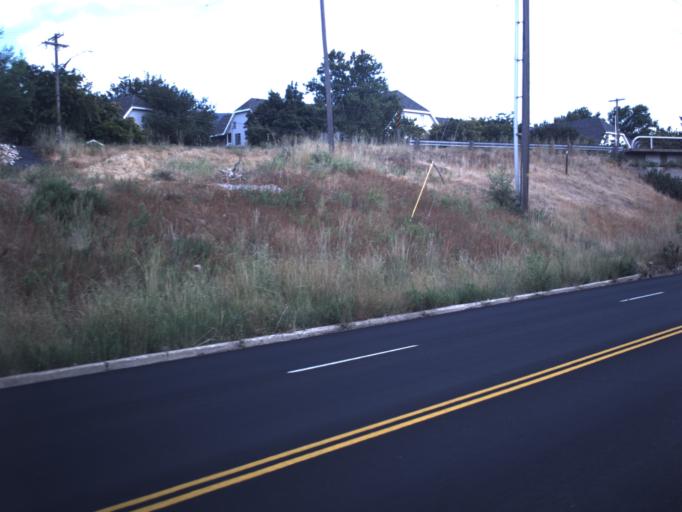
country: US
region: Utah
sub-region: Davis County
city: Woods Cross
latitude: 40.8699
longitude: -111.8923
